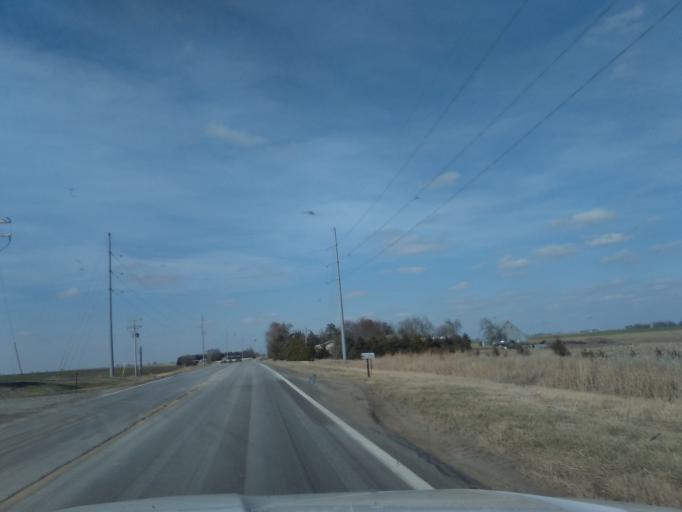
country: US
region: Nebraska
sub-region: Gage County
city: Beatrice
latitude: 40.1999
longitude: -96.9353
